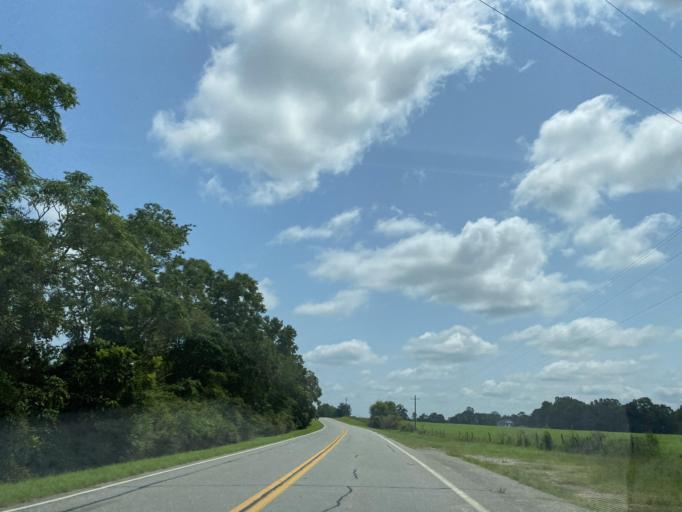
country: US
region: Georgia
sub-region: Telfair County
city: Helena
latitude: 32.0115
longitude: -83.0972
